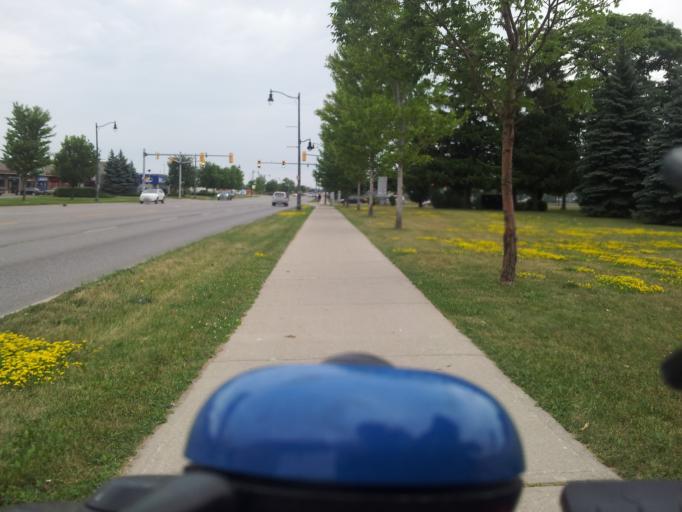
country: CA
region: Ontario
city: Stratford
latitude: 43.3708
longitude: -80.9538
